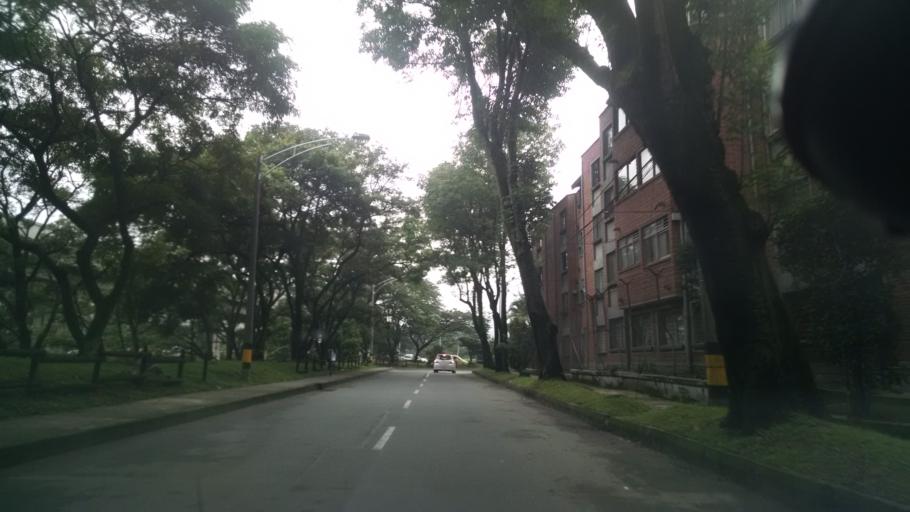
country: CO
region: Antioquia
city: Medellin
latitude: 6.2513
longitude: -75.5805
